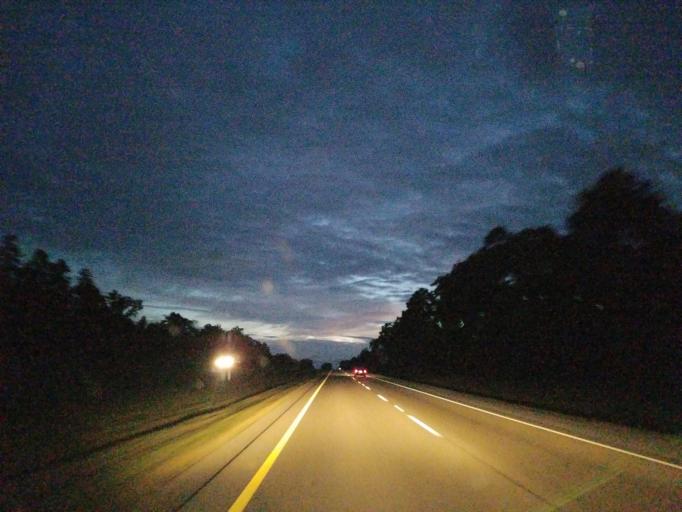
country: US
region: Mississippi
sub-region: Jones County
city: Sharon
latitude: 31.7465
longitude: -89.0799
